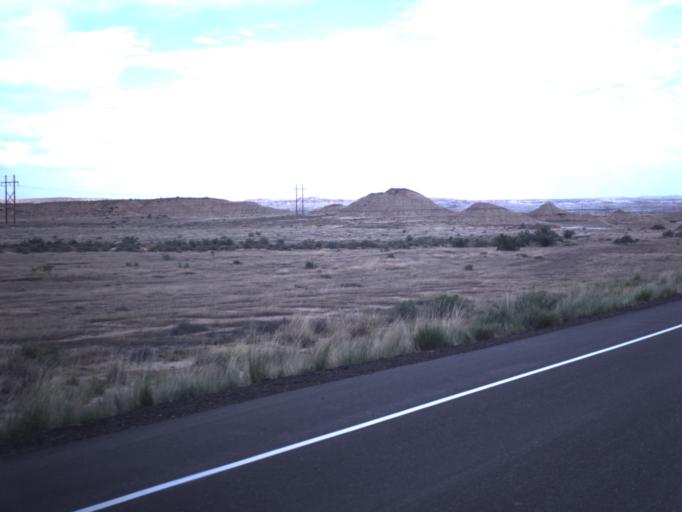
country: US
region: Utah
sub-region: Uintah County
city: Naples
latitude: 40.1218
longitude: -109.2572
